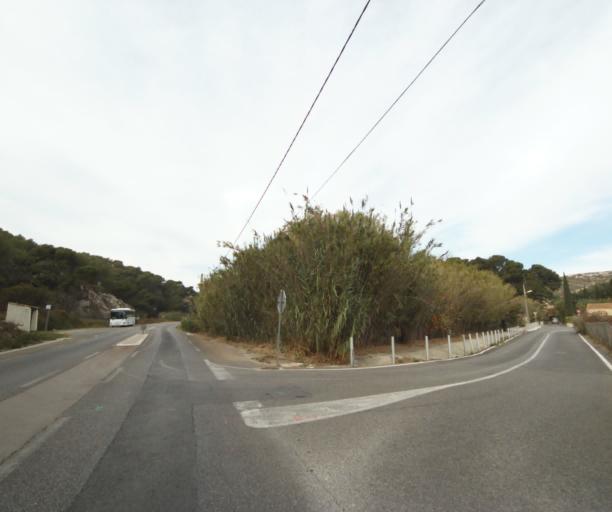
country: FR
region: Provence-Alpes-Cote d'Azur
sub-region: Departement des Bouches-du-Rhone
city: Le Rove
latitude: 43.3680
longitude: 5.2619
